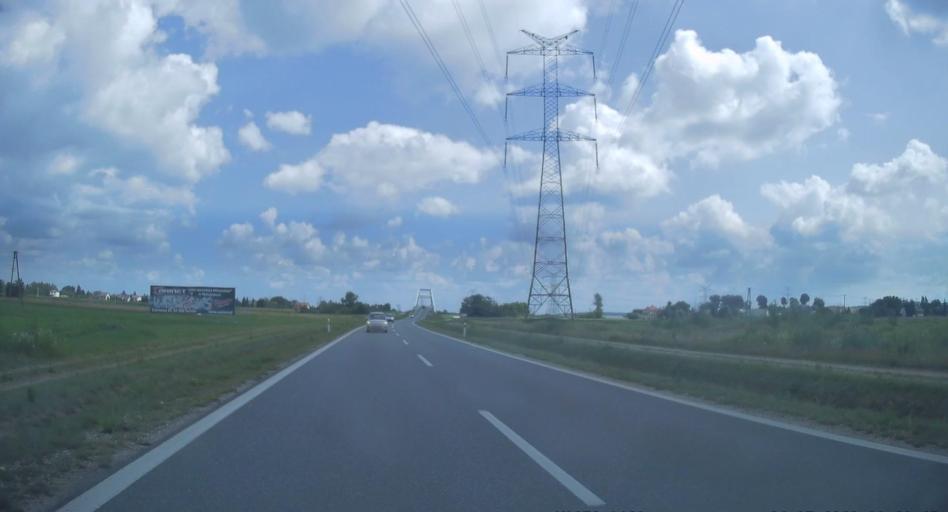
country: PL
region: Lesser Poland Voivodeship
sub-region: Powiat tarnowski
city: Wojnicz
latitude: 49.9473
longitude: 20.8476
